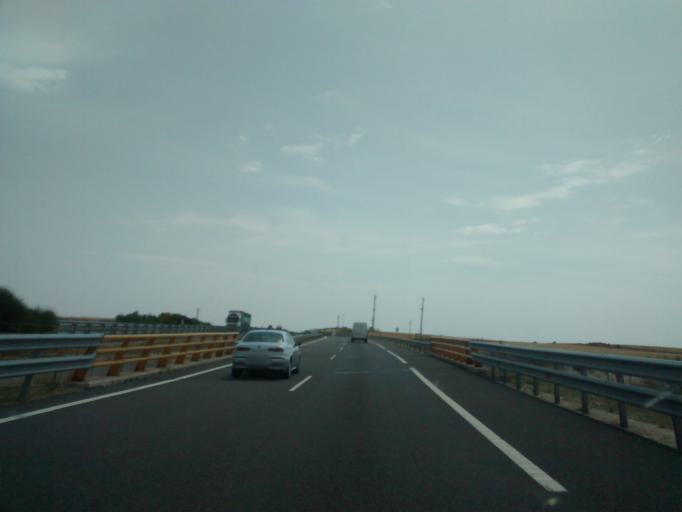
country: ES
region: Castille and Leon
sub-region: Provincia de Burgos
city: Isar
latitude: 42.3684
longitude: -3.8874
